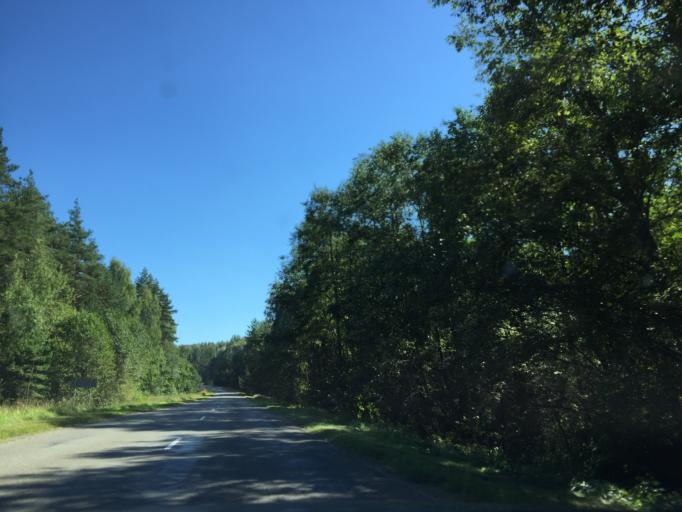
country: LV
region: Akniste
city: Akniste
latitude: 56.1180
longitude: 25.8329
